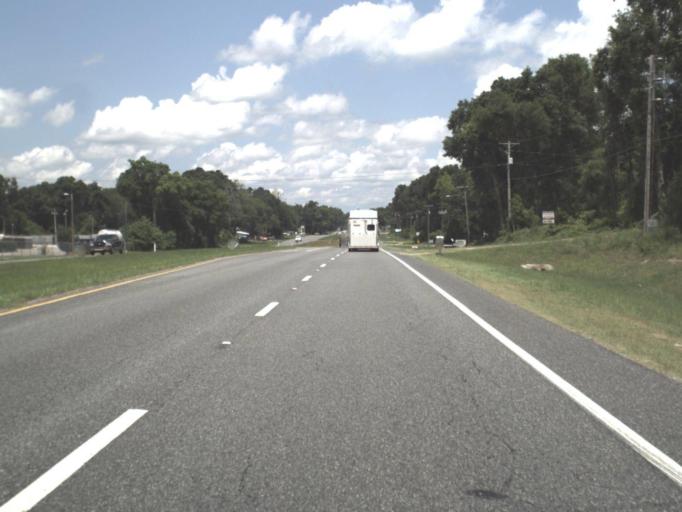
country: US
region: Florida
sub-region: Alachua County
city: High Springs
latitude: 29.8206
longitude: -82.5818
